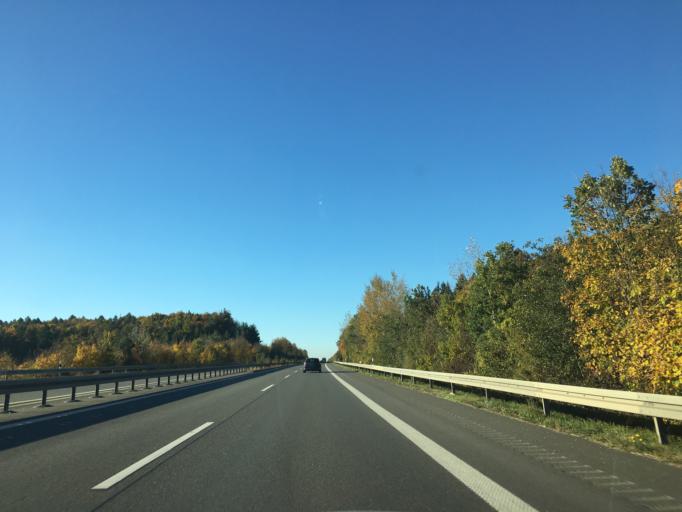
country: DE
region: Baden-Wuerttemberg
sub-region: Freiburg Region
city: Steisslingen
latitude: 47.7775
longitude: 8.9014
